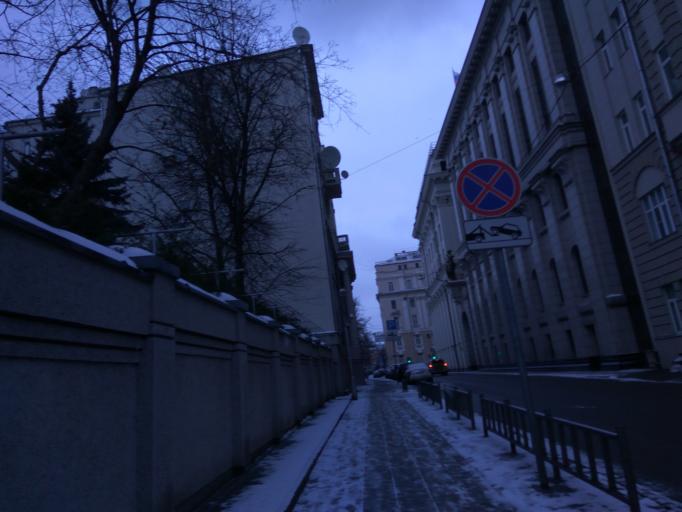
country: RU
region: Moscow
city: Moscow
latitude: 55.7542
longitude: 37.5917
